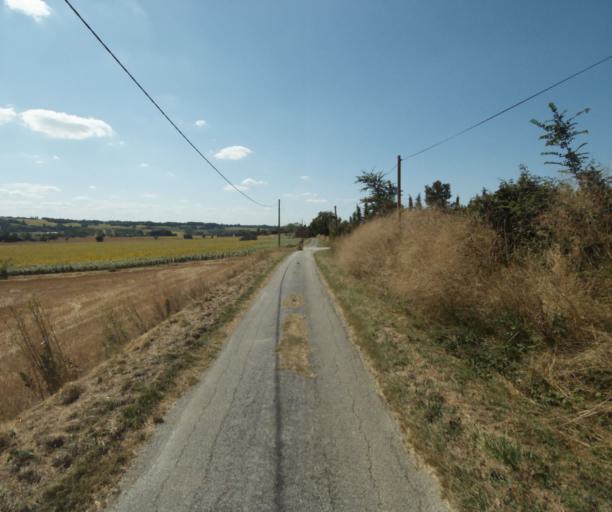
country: FR
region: Midi-Pyrenees
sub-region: Departement de la Haute-Garonne
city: Saint-Felix-Lauragais
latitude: 43.4865
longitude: 1.8951
